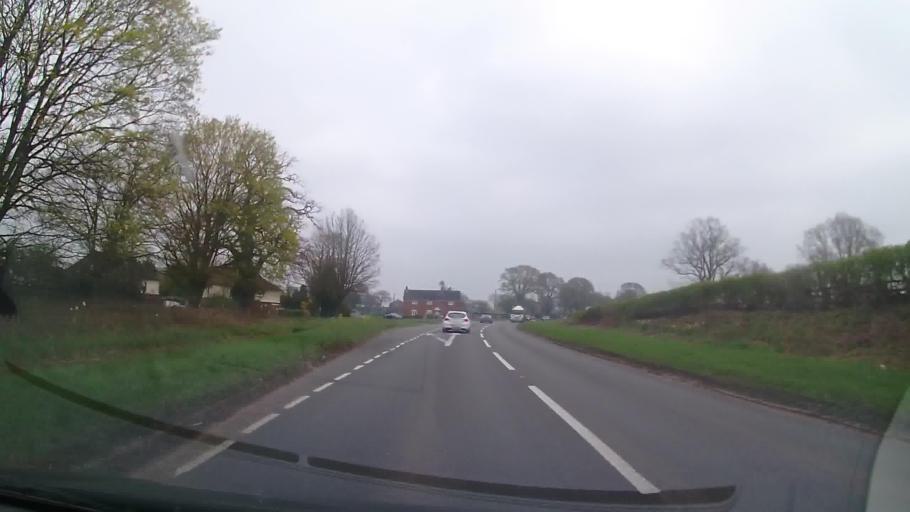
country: GB
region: England
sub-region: Shropshire
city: Market Drayton
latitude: 52.9132
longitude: -2.4449
